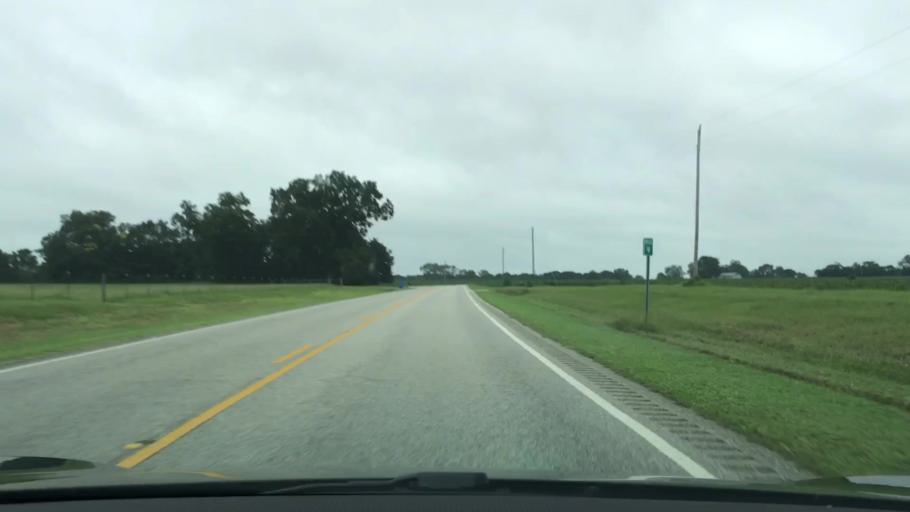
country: US
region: Alabama
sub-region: Coffee County
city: Elba
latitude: 31.3324
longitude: -86.1323
